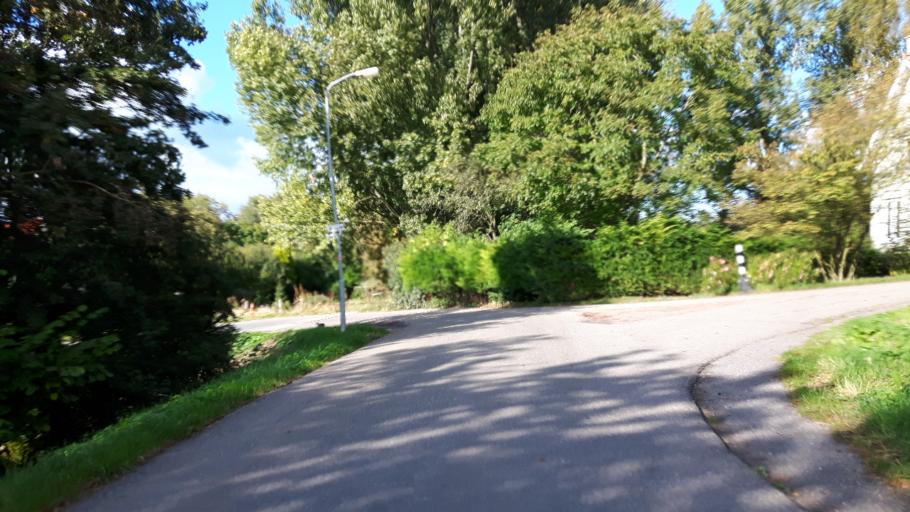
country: NL
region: South Holland
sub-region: Gemeente Leerdam
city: Leerdam
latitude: 51.8725
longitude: 5.0590
